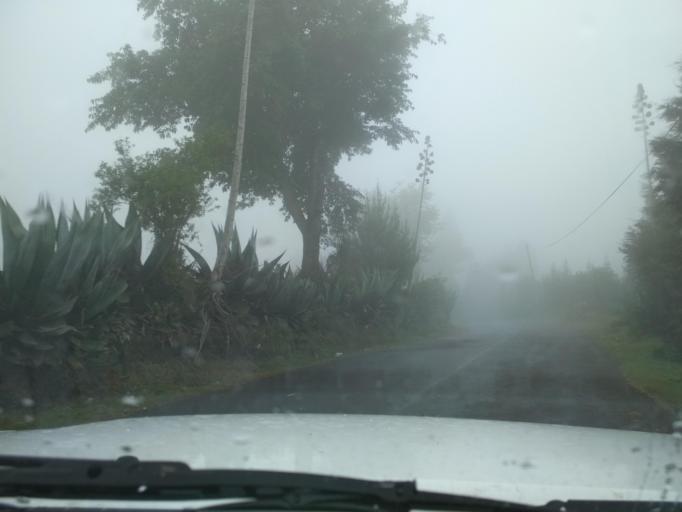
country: MX
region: Veracruz
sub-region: Mariano Escobedo
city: San Isidro el Berro
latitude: 18.9294
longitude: -97.2099
